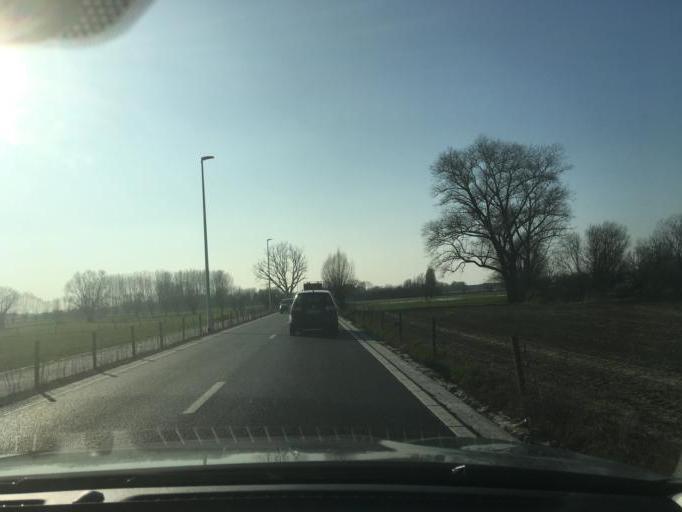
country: BE
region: Flanders
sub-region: Provincie West-Vlaanderen
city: Ledegem
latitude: 50.8713
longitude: 3.1623
